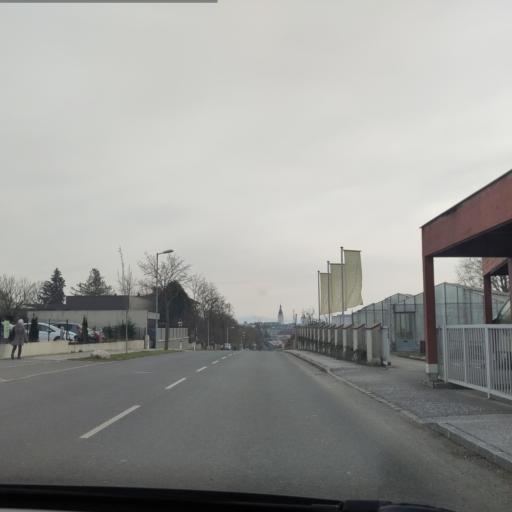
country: AT
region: Lower Austria
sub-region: Sankt Polten Stadt
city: Sankt Poelten
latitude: 48.2130
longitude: 15.6135
